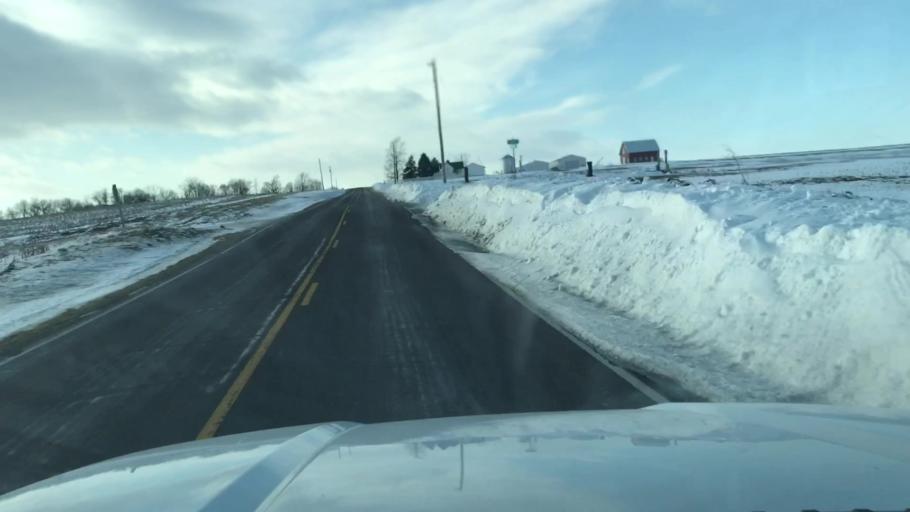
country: US
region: Missouri
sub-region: Nodaway County
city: Maryville
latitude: 40.2013
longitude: -94.9152
